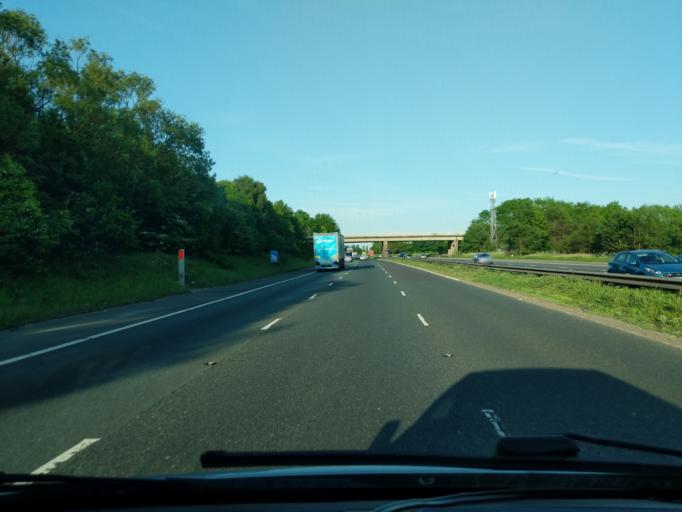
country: GB
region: England
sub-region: Knowsley
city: Whiston
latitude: 53.4004
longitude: -2.7688
